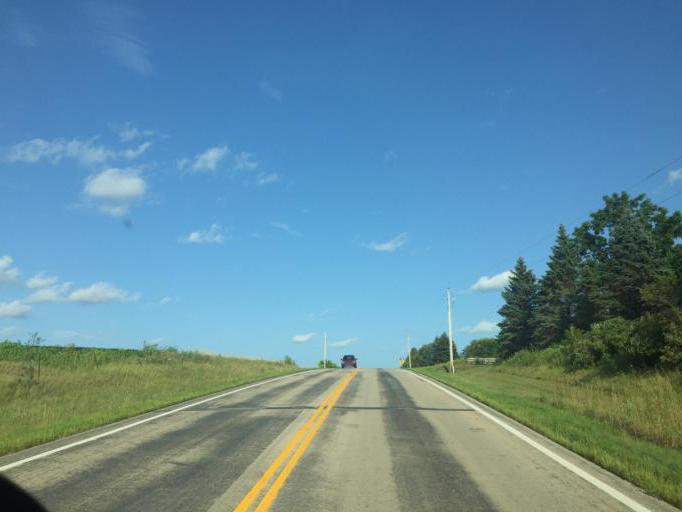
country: US
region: Minnesota
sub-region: Olmsted County
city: Rochester
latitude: 43.9640
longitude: -92.5523
